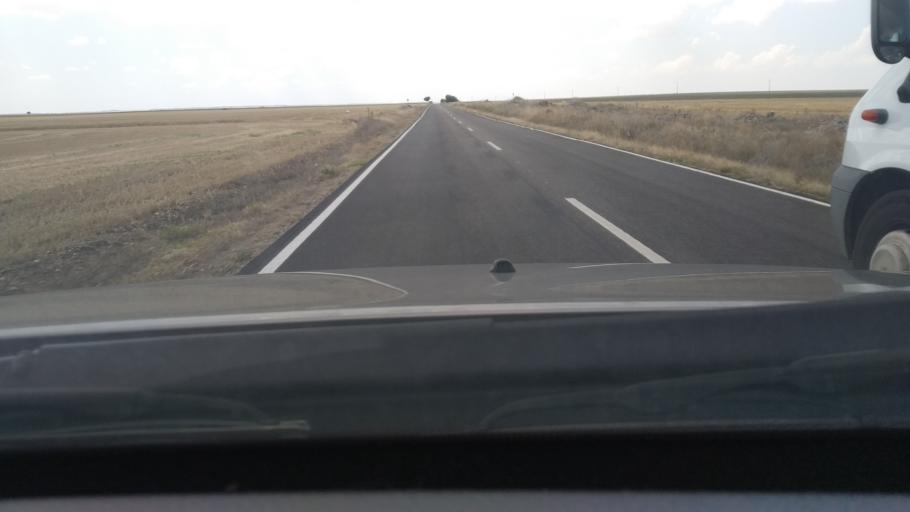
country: ES
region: Castille and Leon
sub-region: Provincia de Burgos
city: Iglesiarrubia
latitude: 41.9461
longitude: -3.8444
